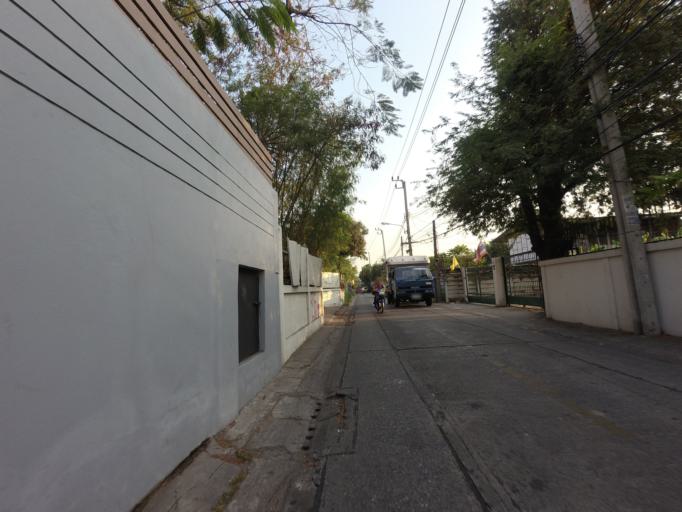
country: TH
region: Bangkok
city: Watthana
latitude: 13.7280
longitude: 100.5910
